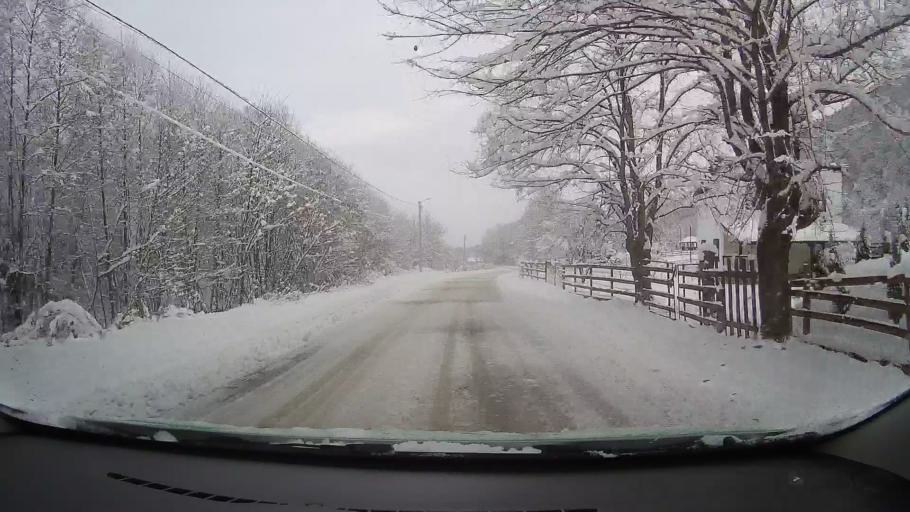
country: RO
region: Alba
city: Pianu de Sus
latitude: 45.8768
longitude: 23.4923
